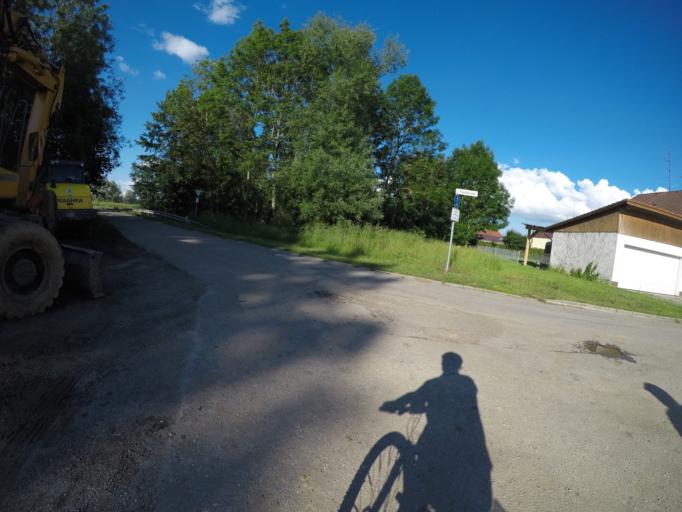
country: DE
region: Bavaria
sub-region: Lower Bavaria
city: Marklkofen
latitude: 48.5576
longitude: 12.5656
